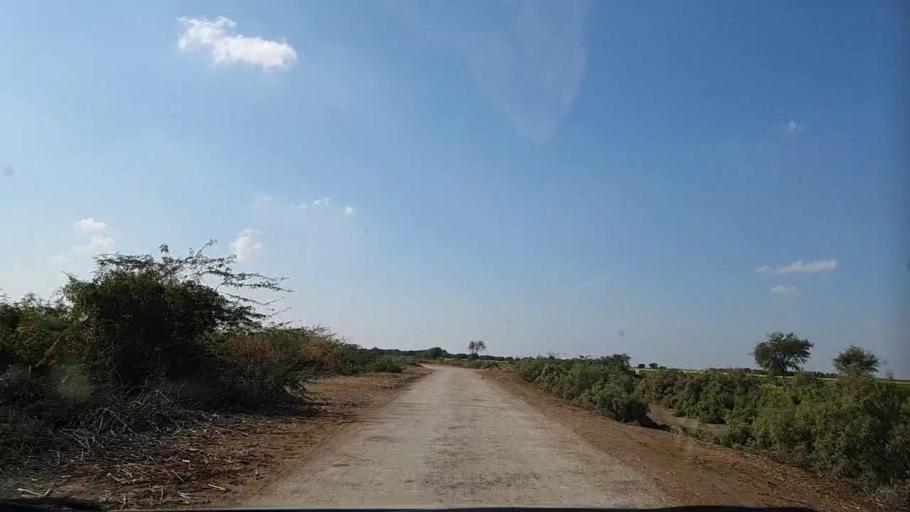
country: PK
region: Sindh
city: Pithoro
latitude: 25.6689
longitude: 69.4631
